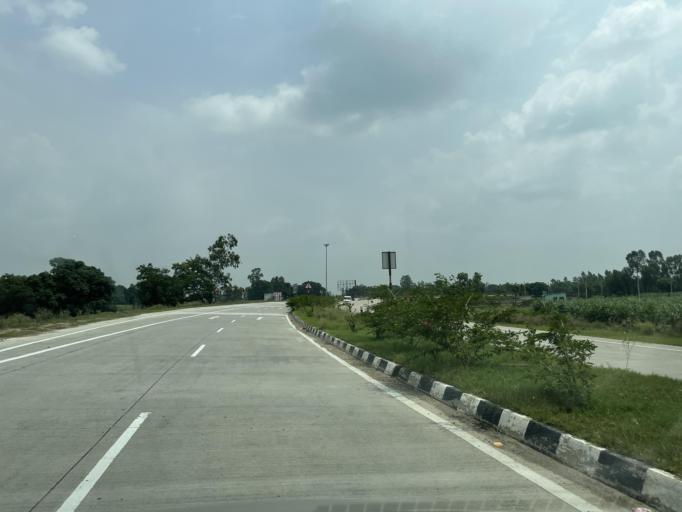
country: IN
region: Uttar Pradesh
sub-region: Bijnor
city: Nagina
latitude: 29.4250
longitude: 78.4423
